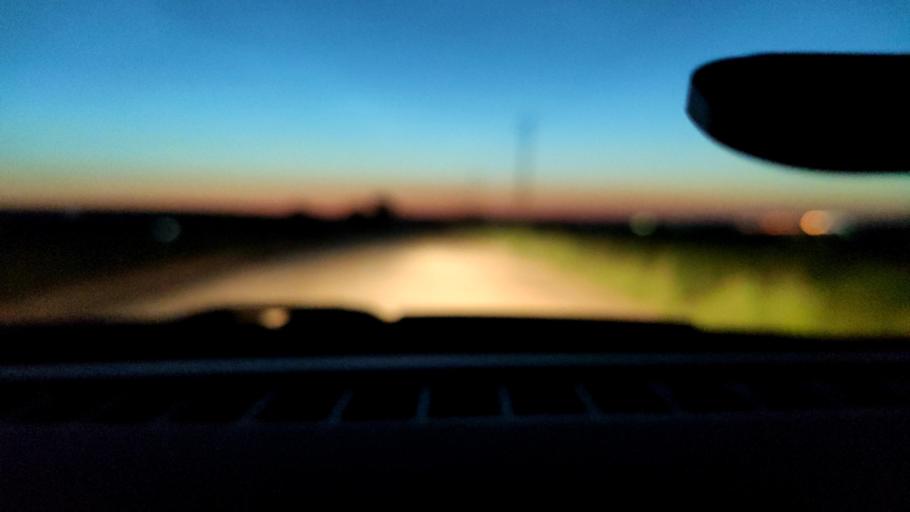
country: RU
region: Perm
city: Kultayevo
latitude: 57.8552
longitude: 55.9841
